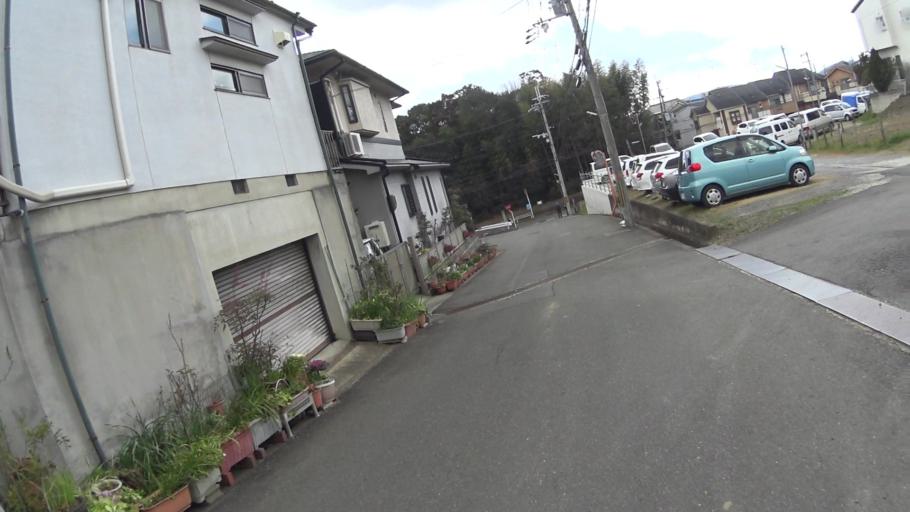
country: JP
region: Kyoto
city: Muko
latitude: 34.9529
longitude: 135.6950
